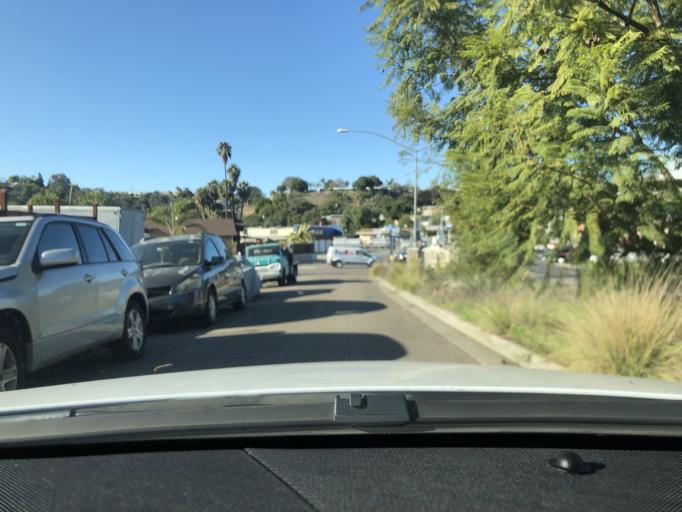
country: US
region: California
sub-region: San Diego County
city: Lemon Grove
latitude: 32.7516
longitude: -117.0639
